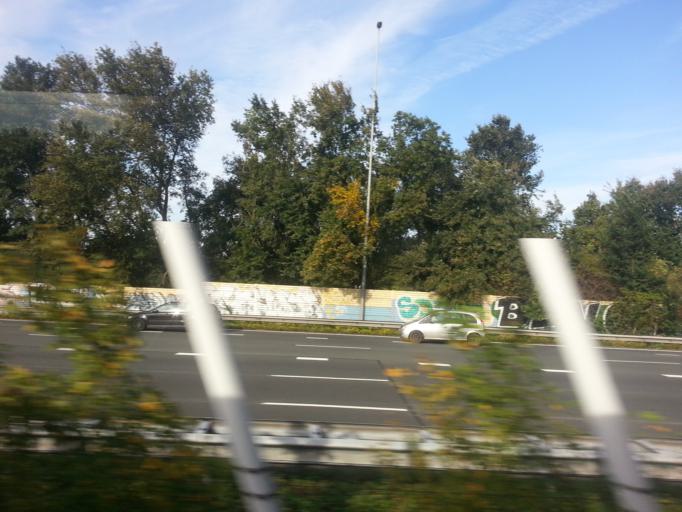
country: NL
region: North Holland
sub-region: Gemeente Amstelveen
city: Amstelveen
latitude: 52.3320
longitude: 4.8011
